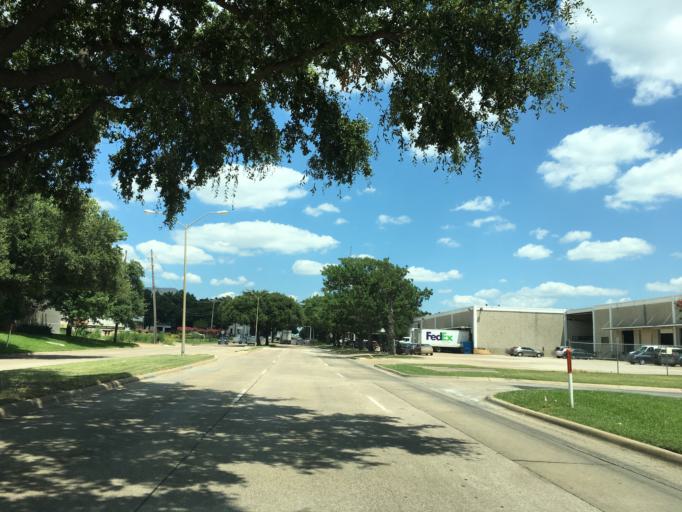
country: US
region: Texas
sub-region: Dallas County
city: Addison
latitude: 32.9396
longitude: -96.8332
